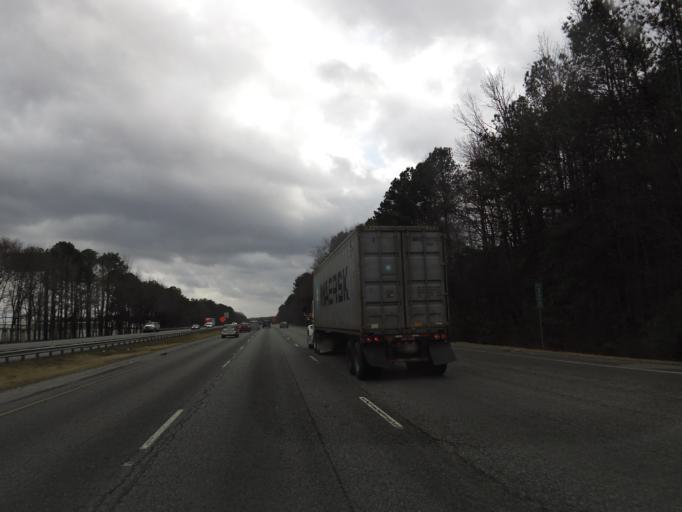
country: US
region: Georgia
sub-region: Whitfield County
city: Dalton
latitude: 34.6823
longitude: -85.0007
